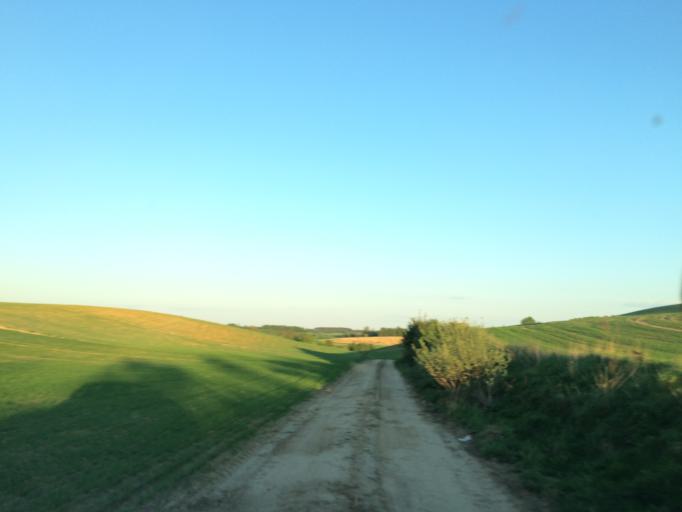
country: PL
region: Warmian-Masurian Voivodeship
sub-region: Powiat ilawski
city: Lubawa
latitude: 53.4880
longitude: 19.8598
